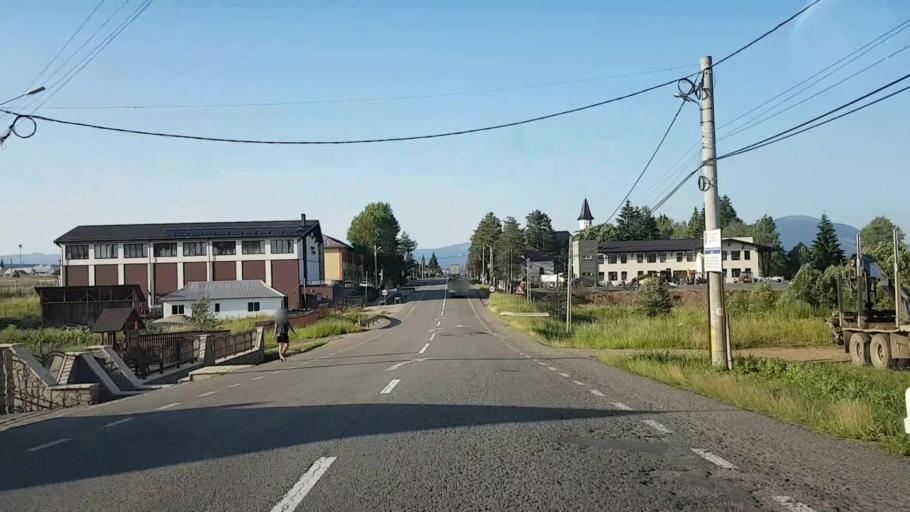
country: RO
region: Suceava
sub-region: Comuna Poiana Stampei
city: Poiana Stampei
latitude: 47.3186
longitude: 25.1352
